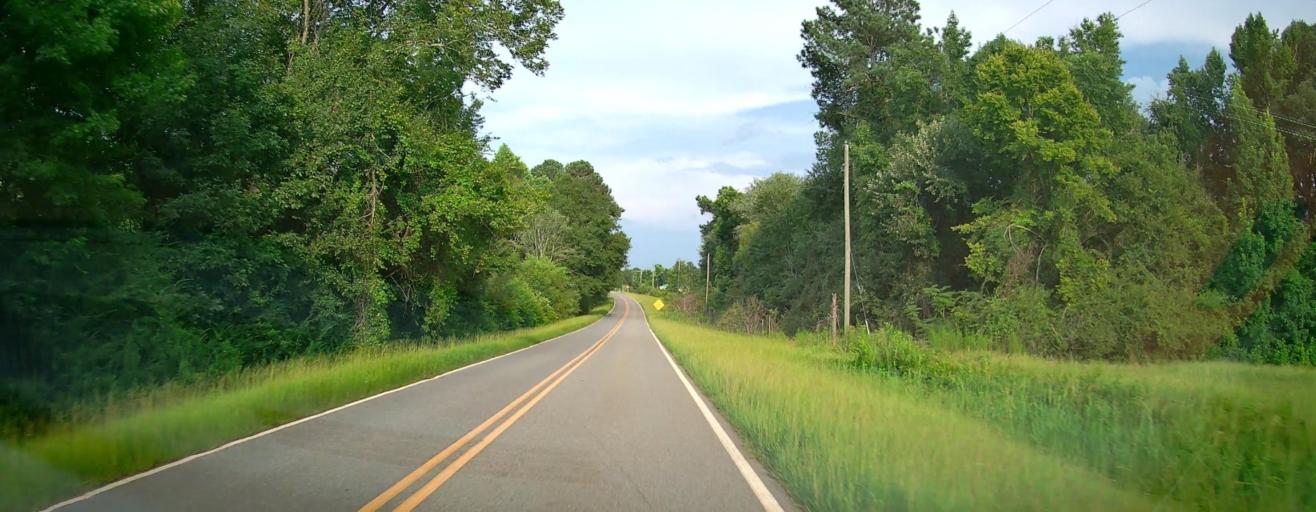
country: US
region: Georgia
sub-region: Laurens County
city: Dublin
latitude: 32.4801
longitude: -82.9596
